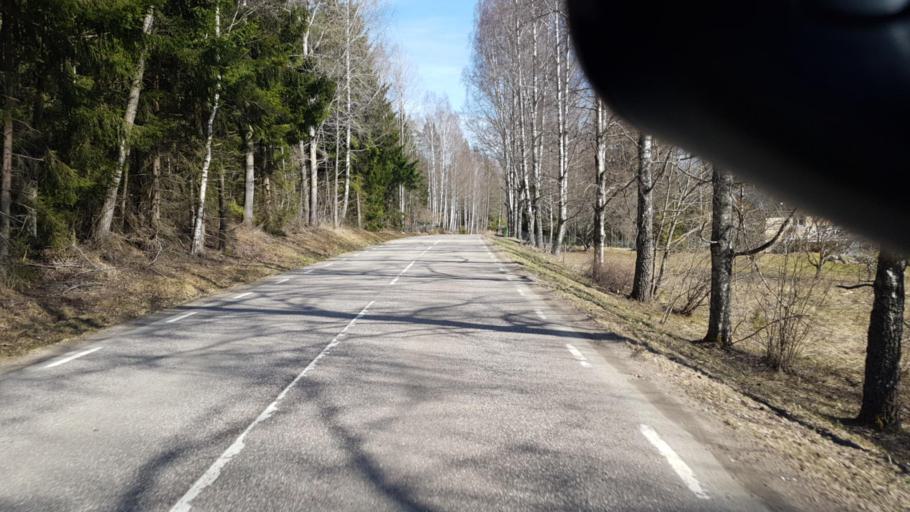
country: SE
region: Vaermland
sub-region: Arvika Kommun
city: Arvika
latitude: 59.6270
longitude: 12.8522
